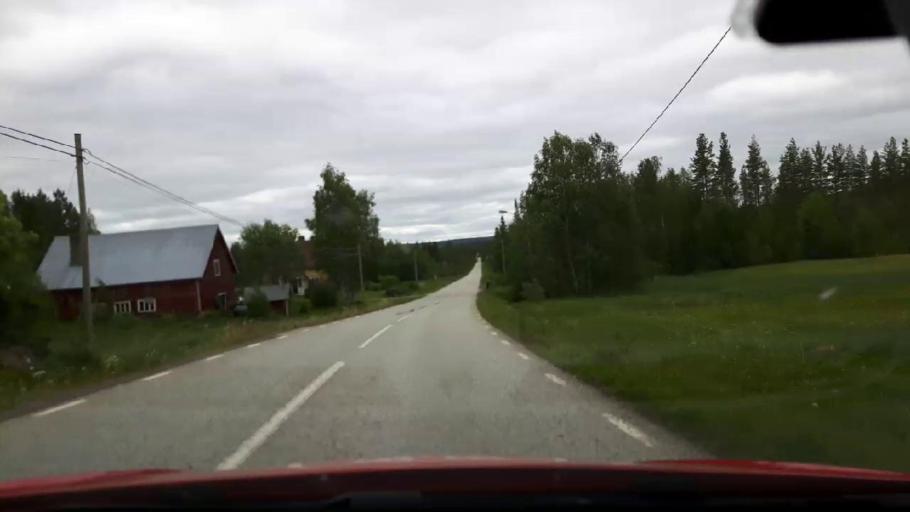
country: SE
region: Jaemtland
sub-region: Stroemsunds Kommun
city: Stroemsund
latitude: 63.3358
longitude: 15.7641
